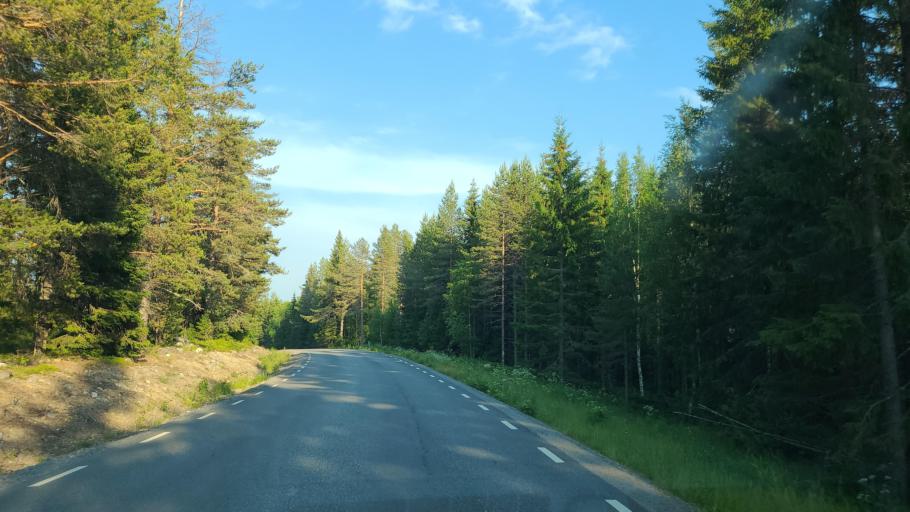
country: SE
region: Vaesterbotten
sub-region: Skelleftea Kommun
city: Burea
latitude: 64.4565
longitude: 21.4240
